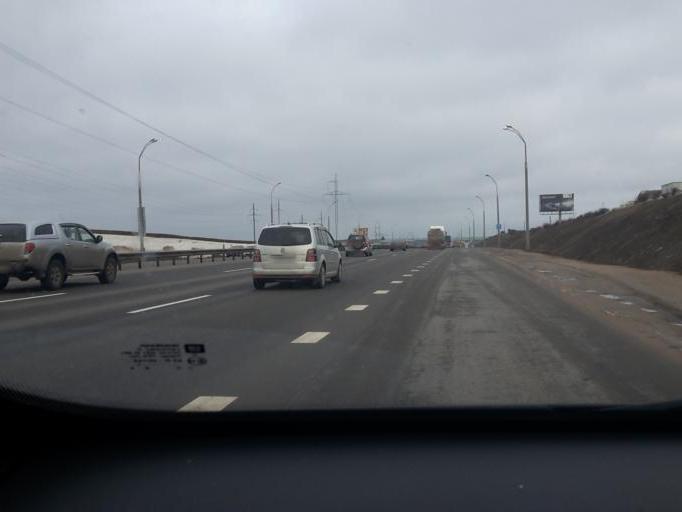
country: BY
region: Minsk
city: Malinovka
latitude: 53.8814
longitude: 27.4171
